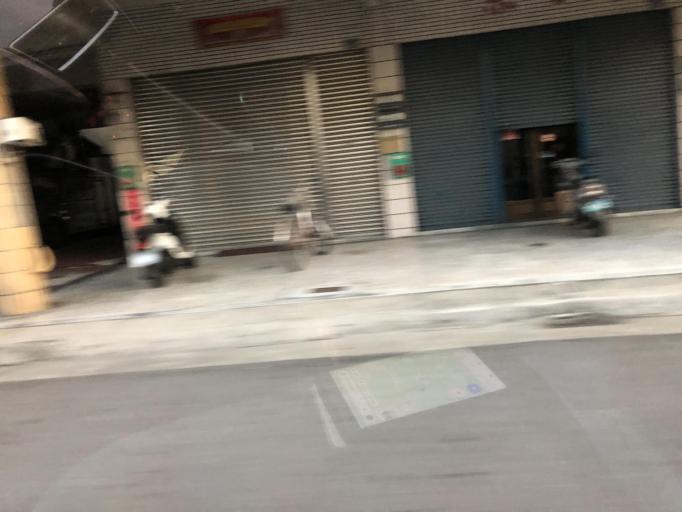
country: TW
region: Taiwan
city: Xinying
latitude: 23.2931
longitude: 120.2761
